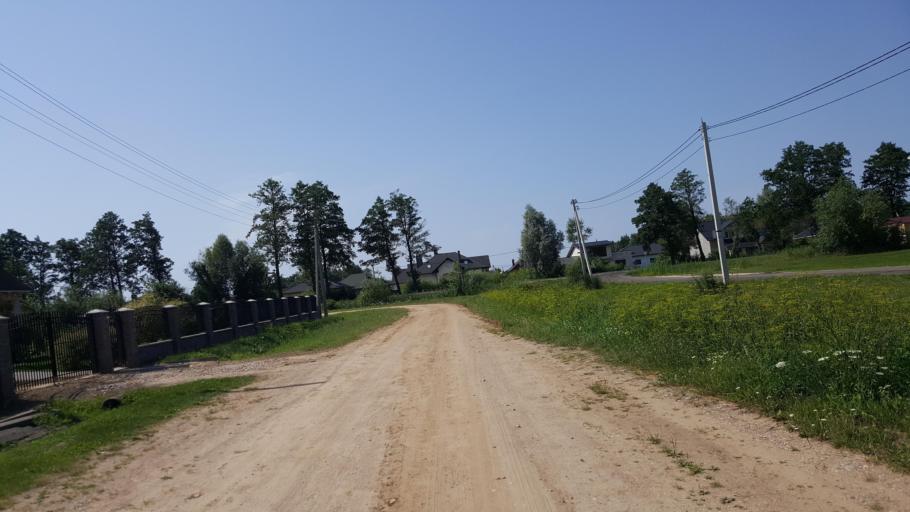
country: BY
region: Brest
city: Zhabinka
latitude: 52.2047
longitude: 23.9985
